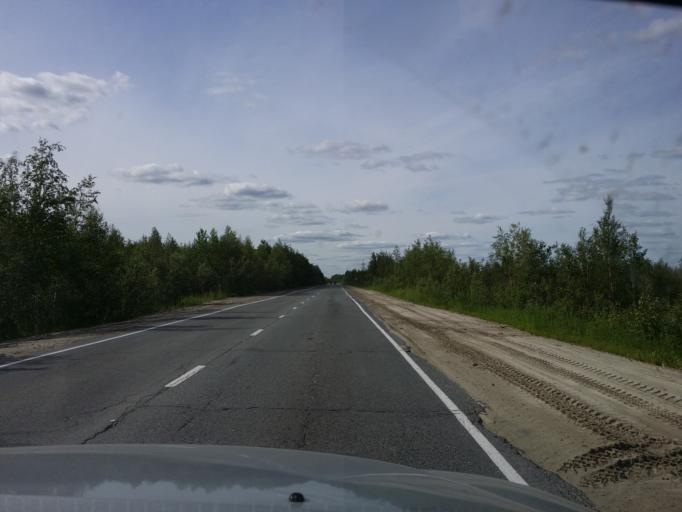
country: RU
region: Khanty-Mansiyskiy Avtonomnyy Okrug
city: Nizhnevartovsk
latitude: 61.1099
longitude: 76.6092
